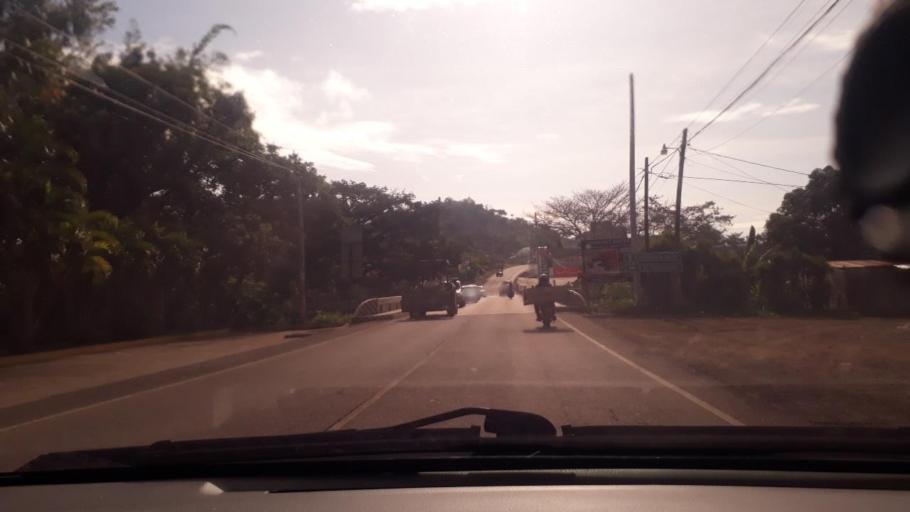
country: GT
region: Jutiapa
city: El Progreso
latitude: 14.3468
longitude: -89.8446
